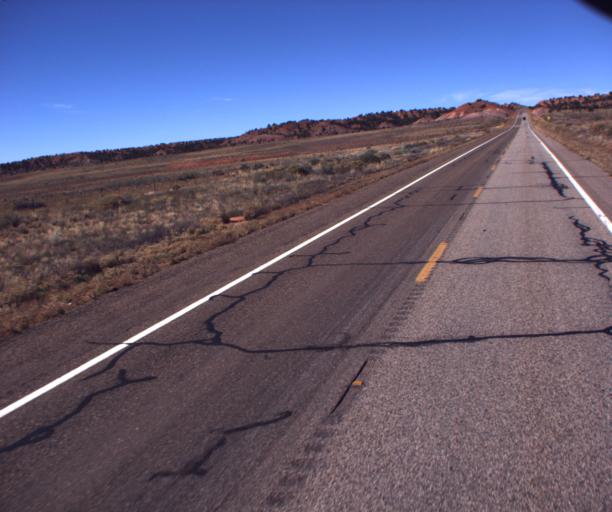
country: US
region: Arizona
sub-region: Mohave County
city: Colorado City
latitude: 36.8775
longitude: -112.8813
